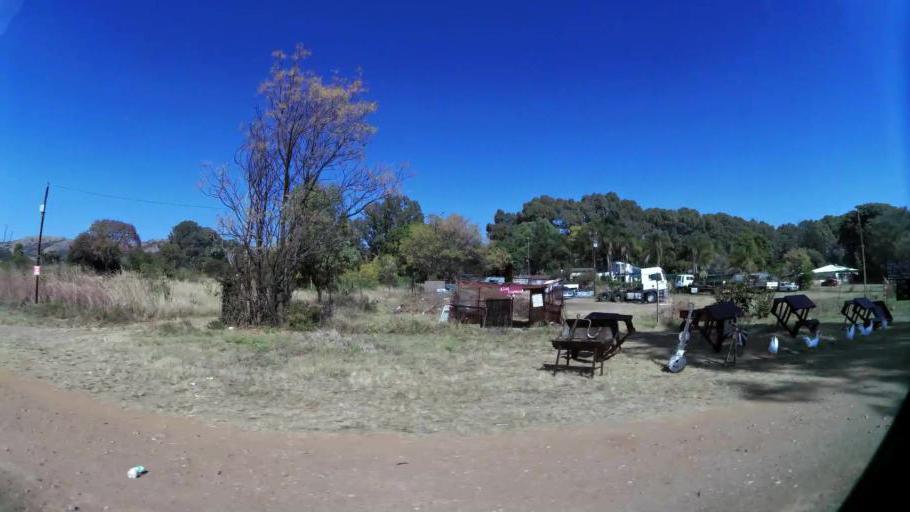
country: ZA
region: North-West
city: Ga-Rankuwa
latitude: -25.6652
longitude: 28.0707
